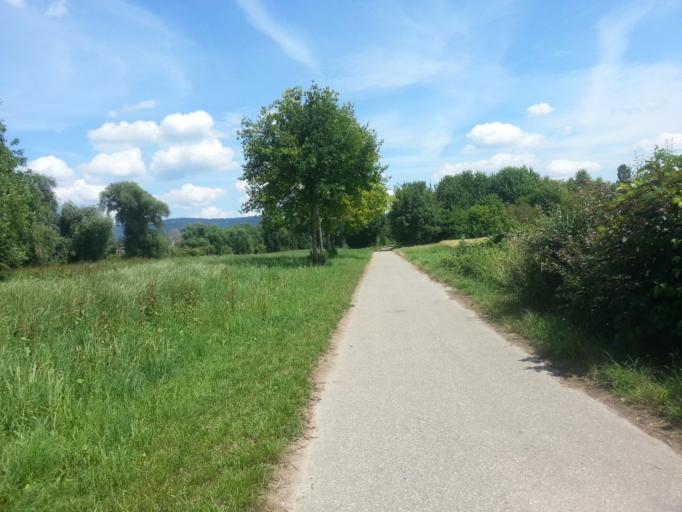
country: DE
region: Baden-Wuerttemberg
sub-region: Karlsruhe Region
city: Edingen-Neckarhausen
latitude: 49.4416
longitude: 8.6315
